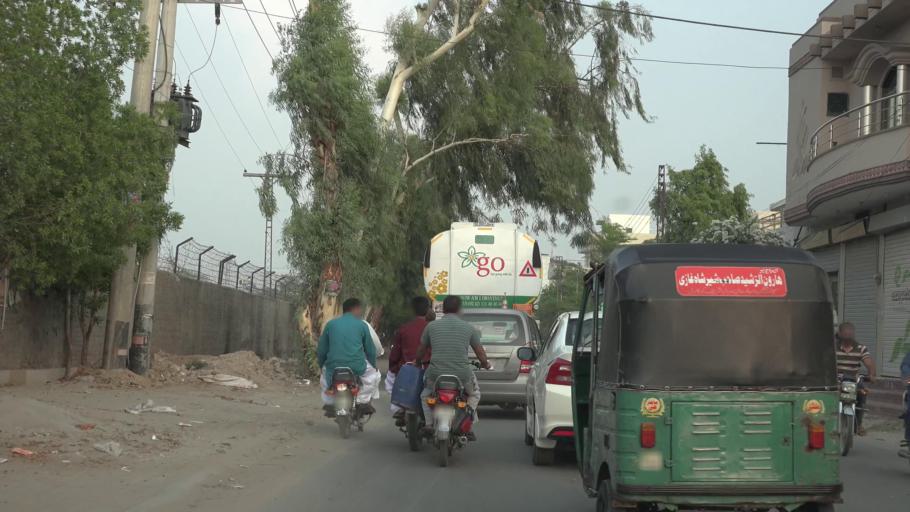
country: PK
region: Punjab
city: Faisalabad
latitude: 31.4454
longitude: 73.1290
